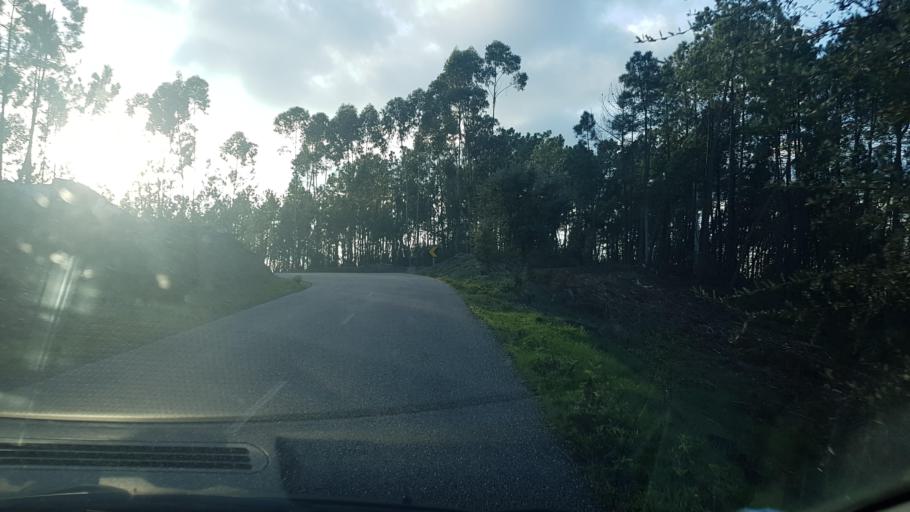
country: PT
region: Castelo Branco
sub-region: Vila de Rei
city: Vila de Rei
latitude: 39.5974
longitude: -8.1199
